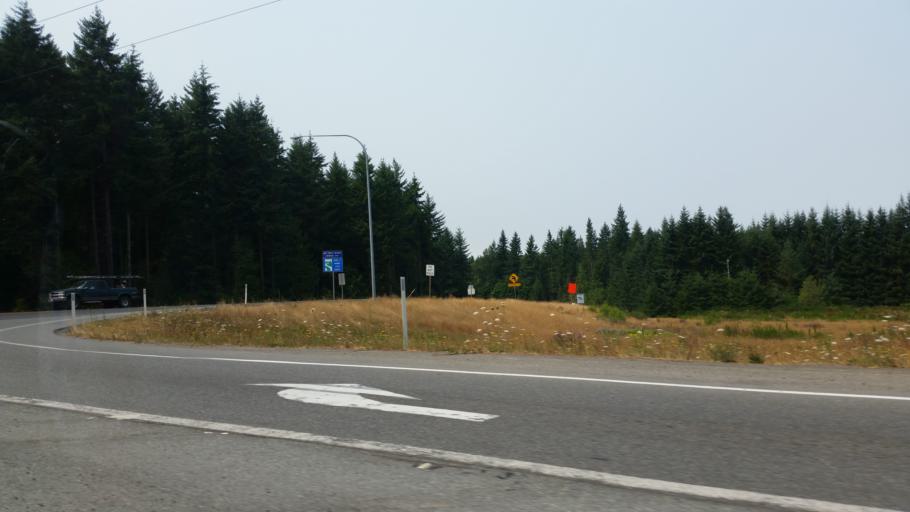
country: US
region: Washington
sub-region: Clallam County
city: Port Angeles
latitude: 48.0977
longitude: -123.5394
